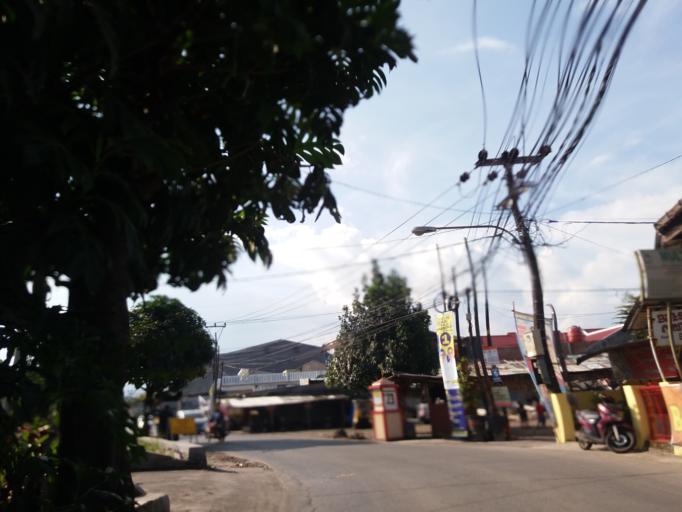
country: ID
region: West Java
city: Bandung
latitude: -6.9256
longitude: 107.6655
